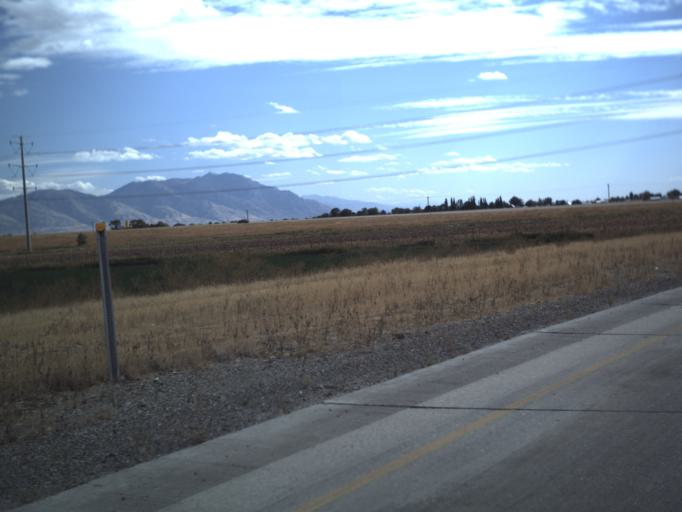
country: US
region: Utah
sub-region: Box Elder County
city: Tremonton
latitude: 41.7012
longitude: -112.1880
